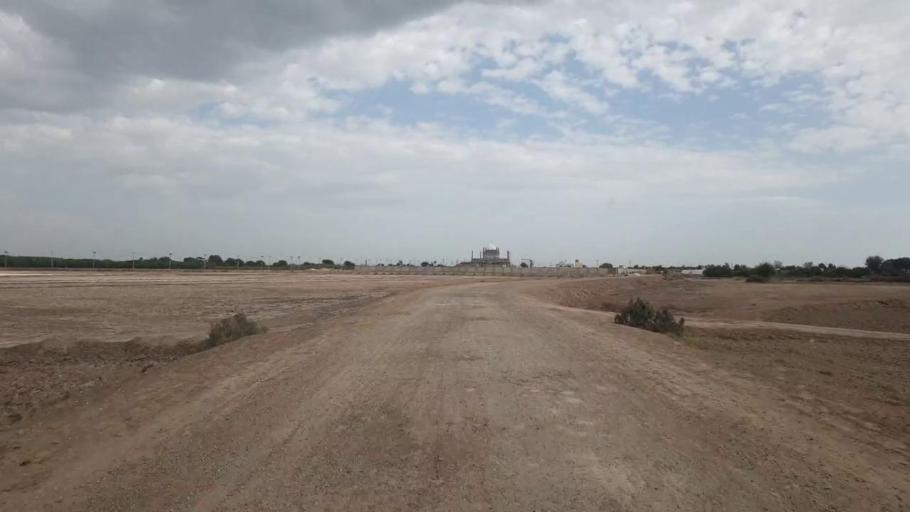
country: PK
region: Sindh
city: Hala
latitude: 25.9341
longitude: 68.3997
